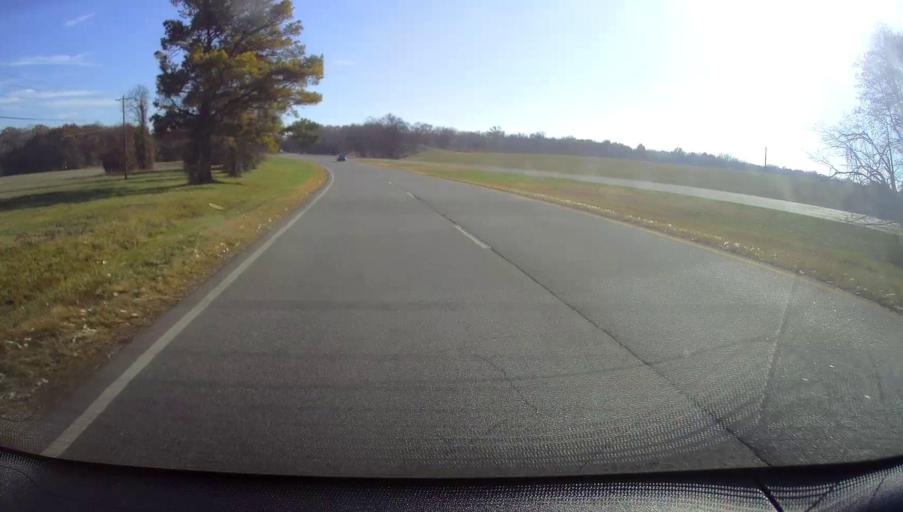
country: US
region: Alabama
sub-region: Morgan County
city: Decatur
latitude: 34.6930
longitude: -86.9553
